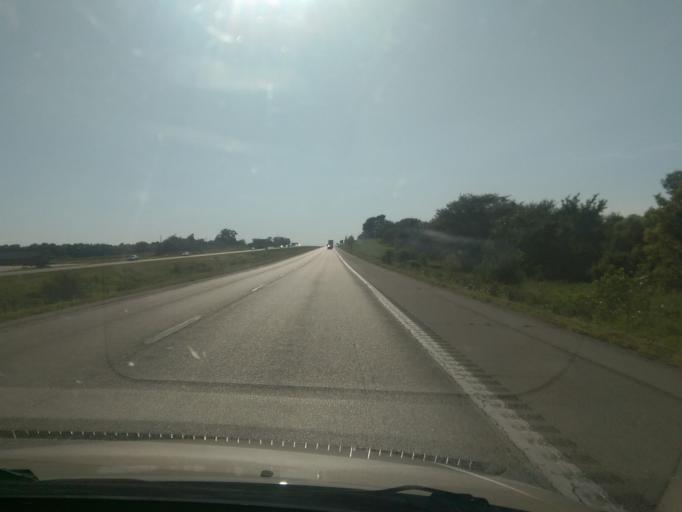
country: US
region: Missouri
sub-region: Lafayette County
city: Odessa
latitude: 39.0107
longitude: -94.0377
